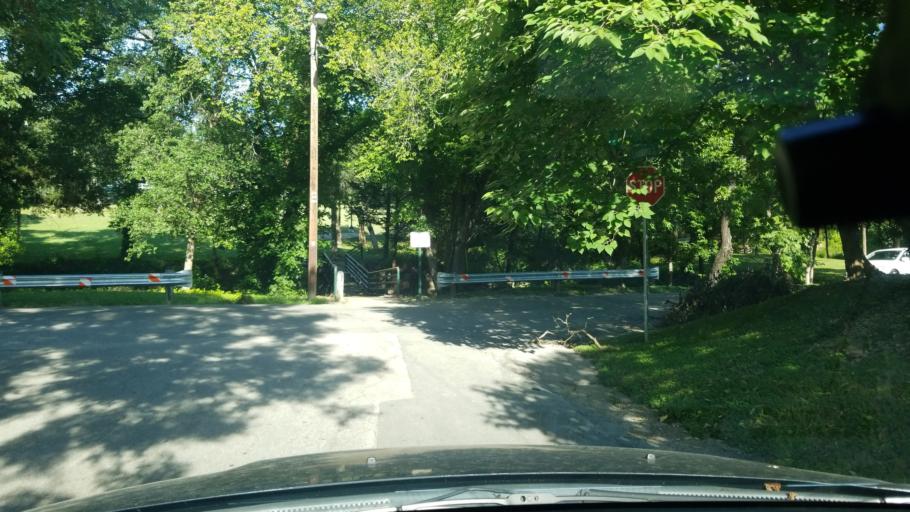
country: US
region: Texas
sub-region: Dallas County
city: Dallas
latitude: 32.7239
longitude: -96.8179
